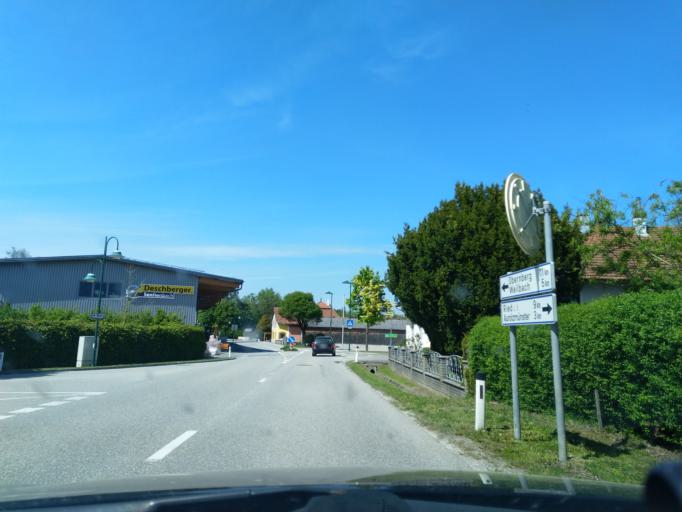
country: AT
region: Upper Austria
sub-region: Politischer Bezirk Ried im Innkreis
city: Ried im Innkreis
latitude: 48.2622
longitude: 13.4189
